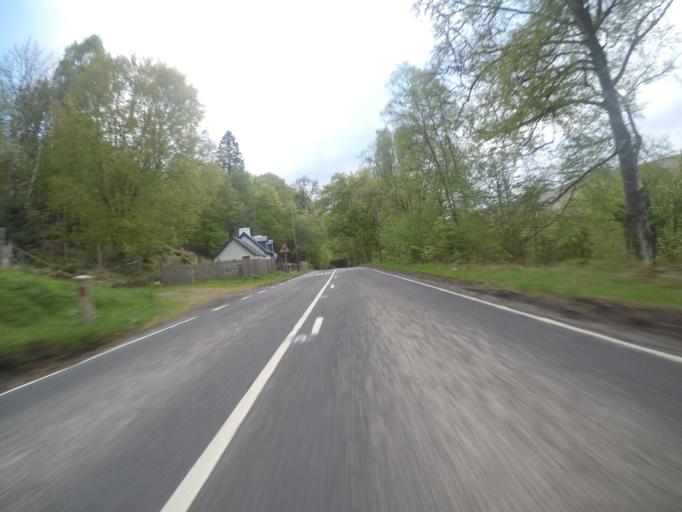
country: GB
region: Scotland
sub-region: Highland
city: Spean Bridge
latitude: 57.0709
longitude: -4.7840
